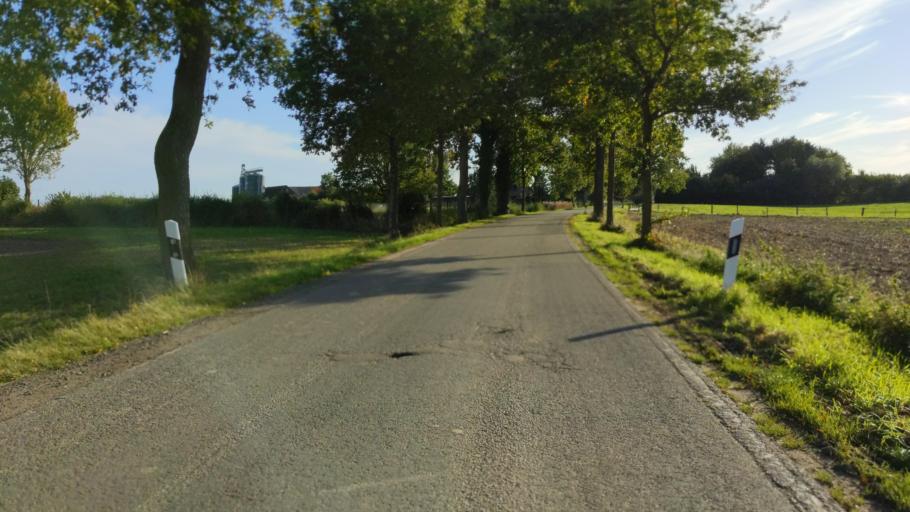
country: DE
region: Schleswig-Holstein
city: Ahrensbok
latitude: 54.0377
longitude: 10.6016
